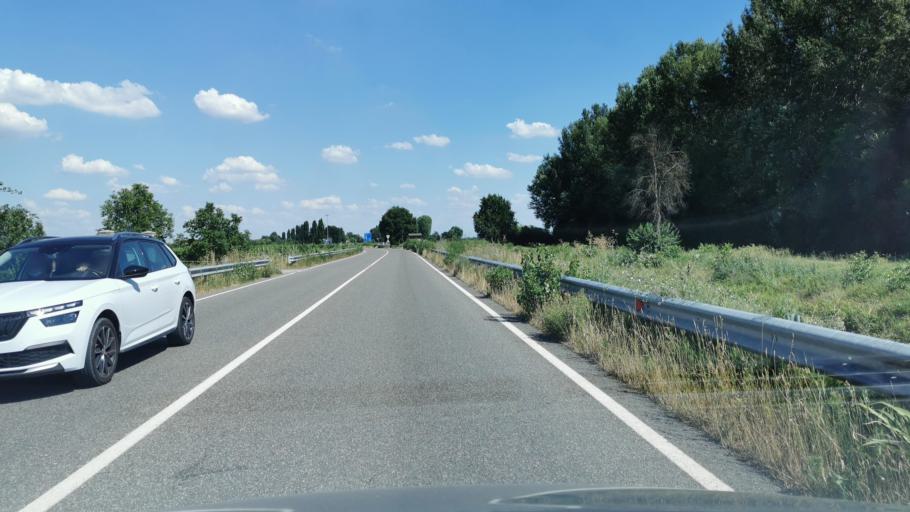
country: IT
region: Emilia-Romagna
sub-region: Provincia di Modena
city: Sam Marino
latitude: 44.7989
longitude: 10.9108
